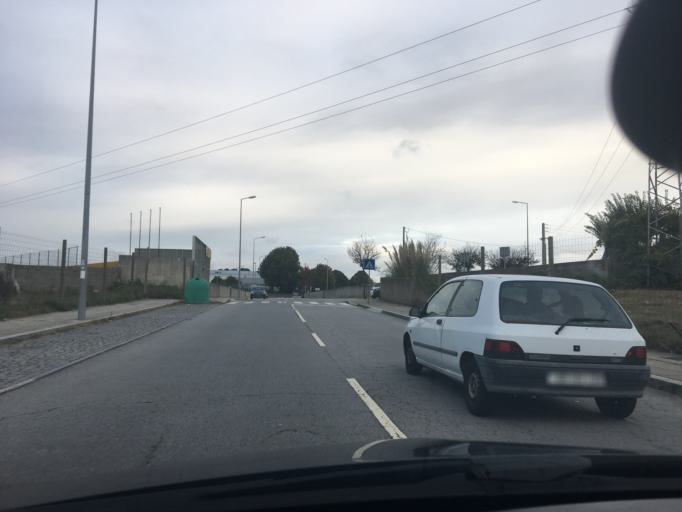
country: PT
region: Porto
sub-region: Matosinhos
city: Santa Cruz do Bispo
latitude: 41.2158
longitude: -8.6772
